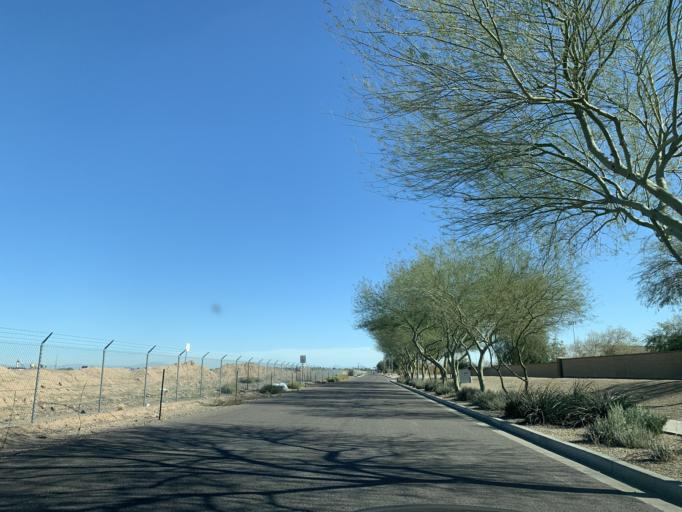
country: US
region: Arizona
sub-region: Maricopa County
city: Laveen
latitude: 33.3994
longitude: -112.1306
